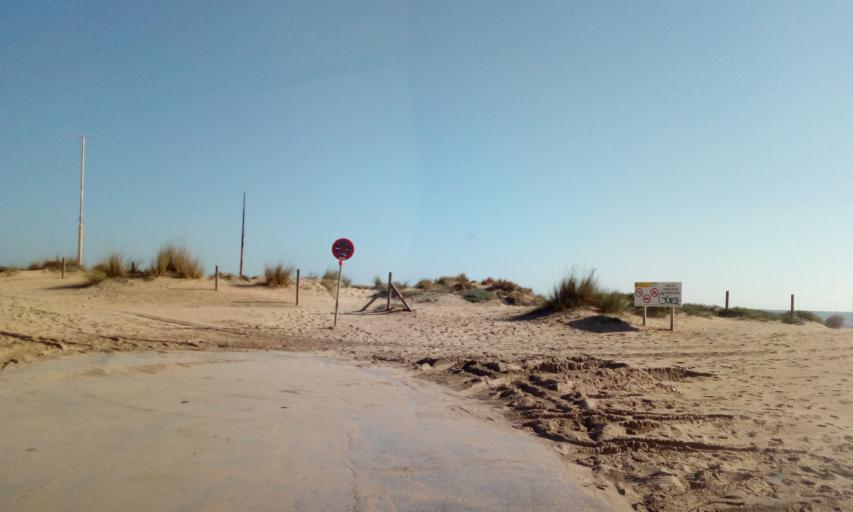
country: ES
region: Andalusia
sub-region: Provincia de Huelva
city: Lepe
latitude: 37.2064
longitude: -7.1976
